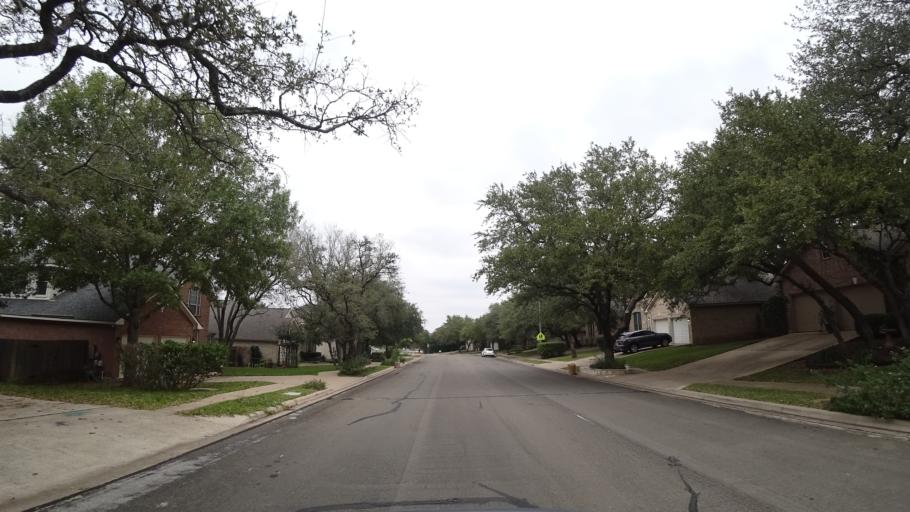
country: US
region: Texas
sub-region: Travis County
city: Shady Hollow
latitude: 30.2092
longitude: -97.8799
